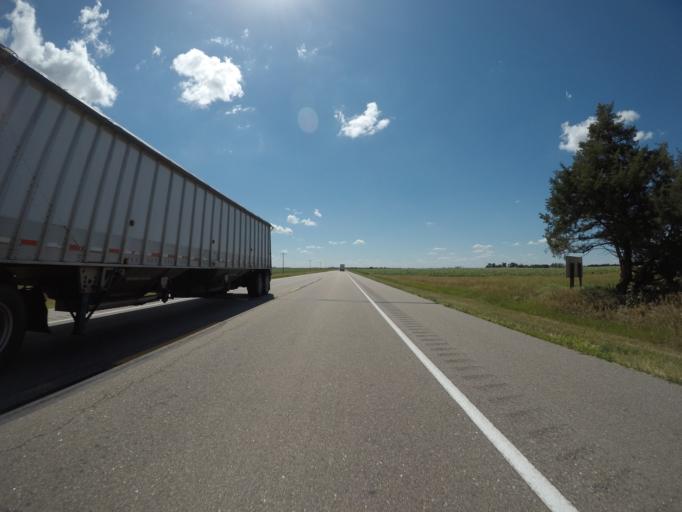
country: US
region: Nebraska
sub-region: Chase County
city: Imperial
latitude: 40.4944
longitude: -101.5826
